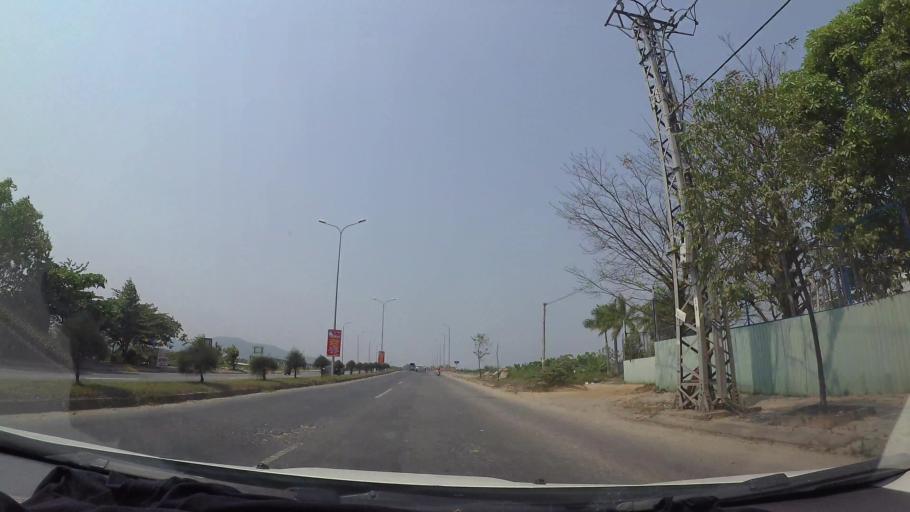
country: VN
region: Da Nang
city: Cam Le
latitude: 15.9976
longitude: 108.1916
